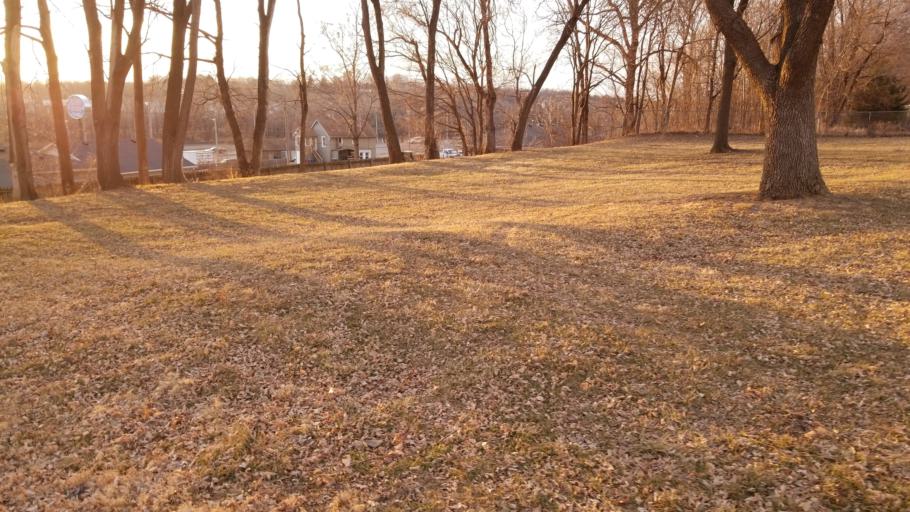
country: US
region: Nebraska
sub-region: Sarpy County
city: Bellevue
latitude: 41.1859
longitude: -95.9308
